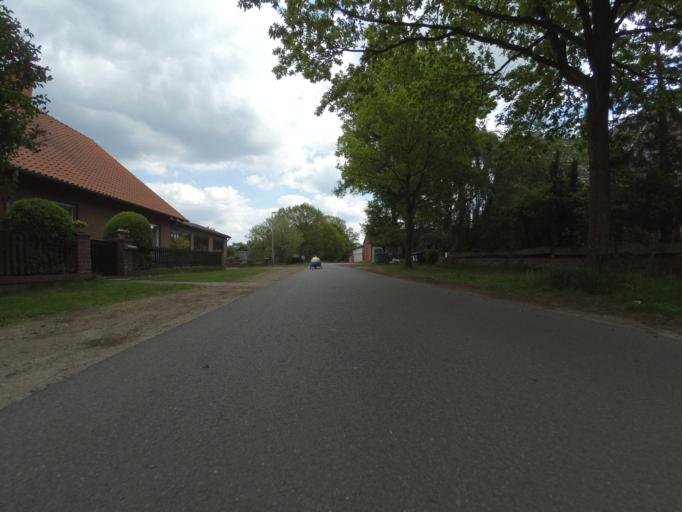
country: DE
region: Lower Saxony
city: Wietze
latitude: 52.5654
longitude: 9.8581
